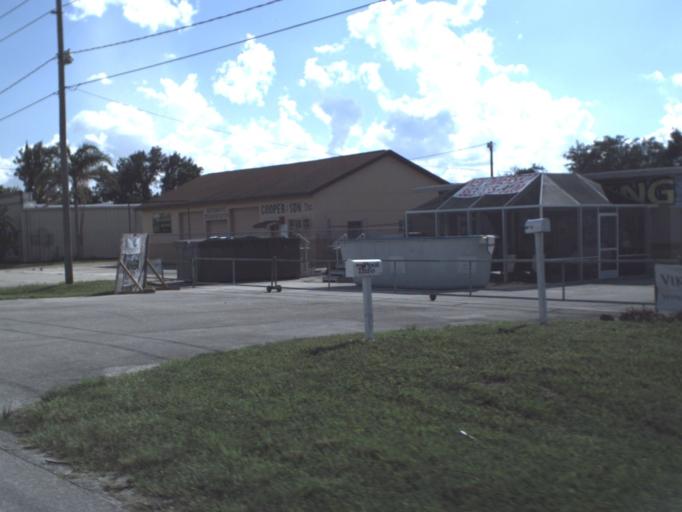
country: US
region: Florida
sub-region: Highlands County
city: Sebring
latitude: 27.4472
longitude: -81.4199
